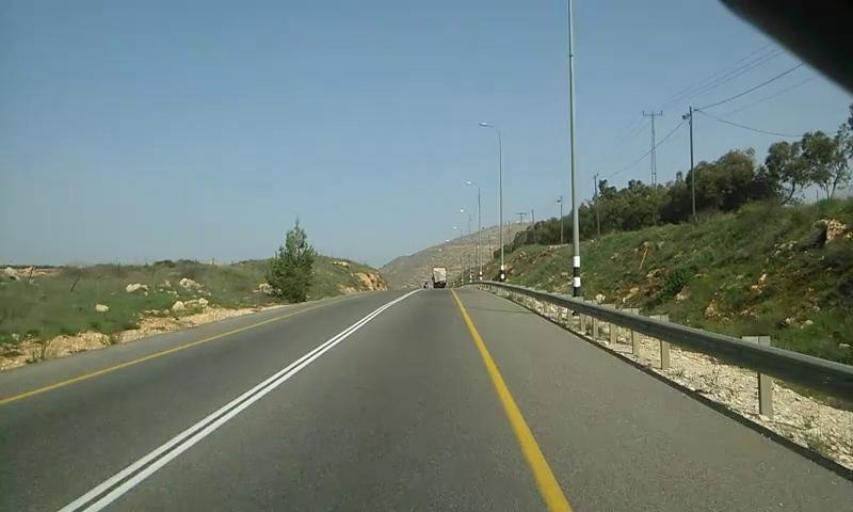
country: PS
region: West Bank
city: Qaryut
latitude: 32.0561
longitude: 35.2863
